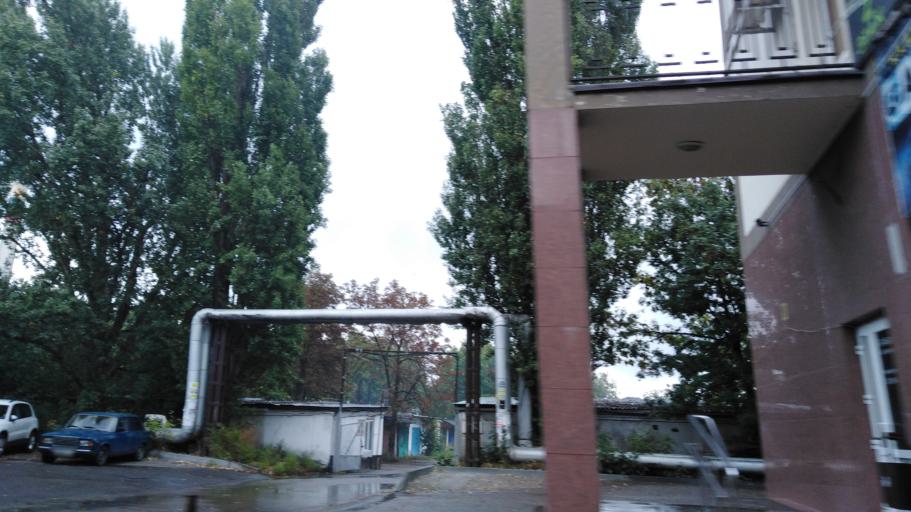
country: RU
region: Stavropol'skiy
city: Yessentukskaya
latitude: 44.0475
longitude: 42.8967
